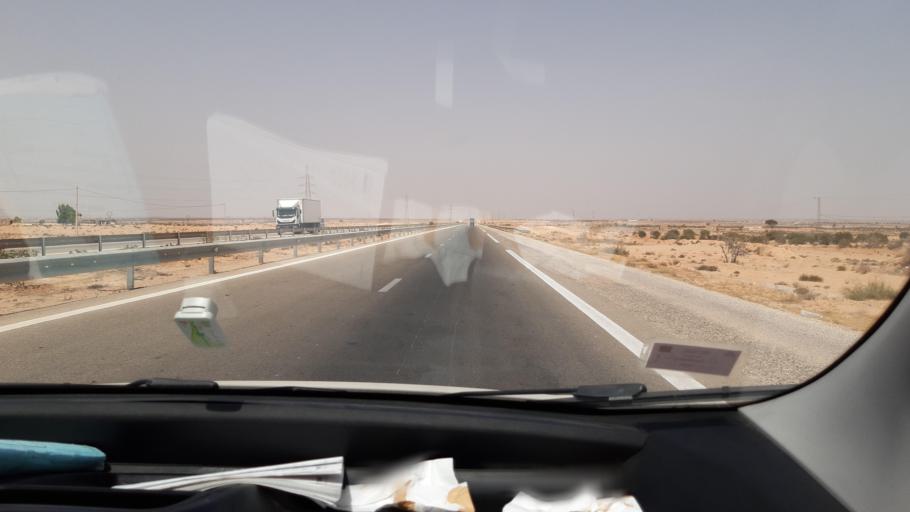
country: TN
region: Safaqis
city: Skhira
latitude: 34.1699
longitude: 9.9739
